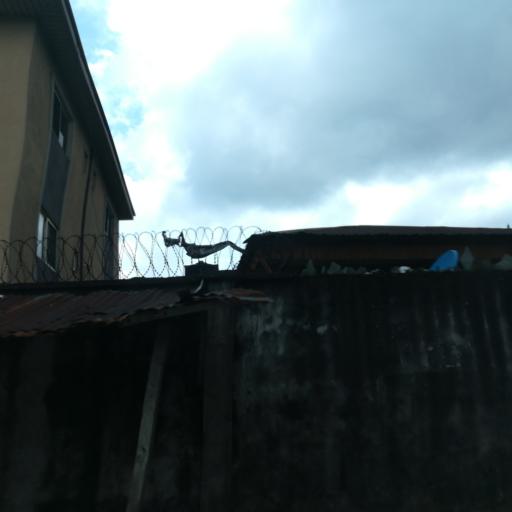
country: NG
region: Rivers
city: Port Harcourt
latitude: 4.8123
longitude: 7.0596
